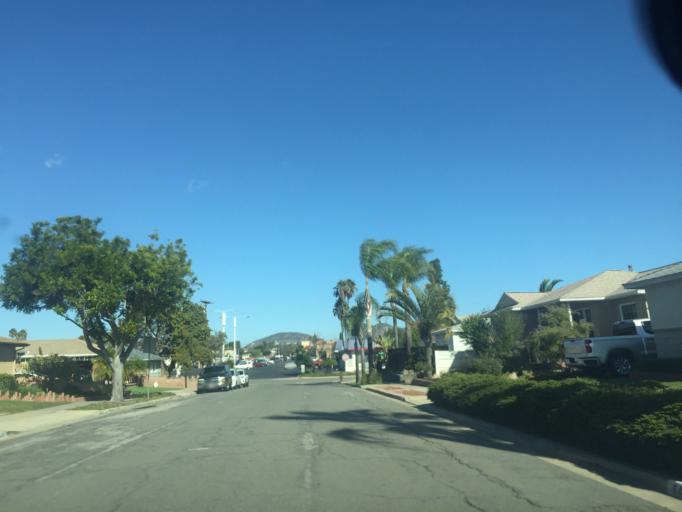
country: US
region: California
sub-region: San Diego County
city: La Mesa
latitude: 32.7897
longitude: -117.0826
